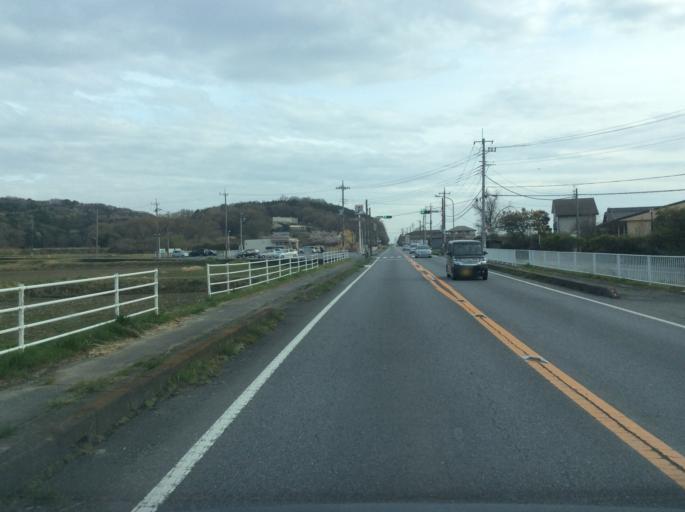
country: JP
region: Ibaraki
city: Tsukuba
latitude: 36.1675
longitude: 140.1067
